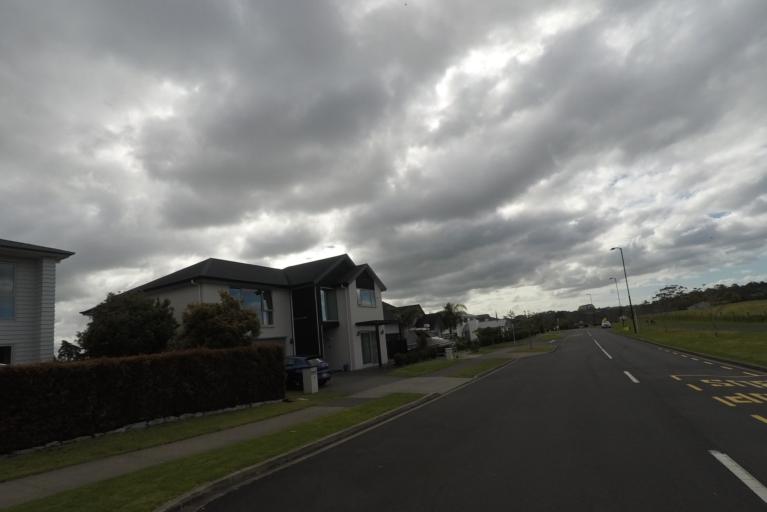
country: NZ
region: Auckland
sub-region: Auckland
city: Rothesay Bay
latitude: -36.6024
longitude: 174.6688
